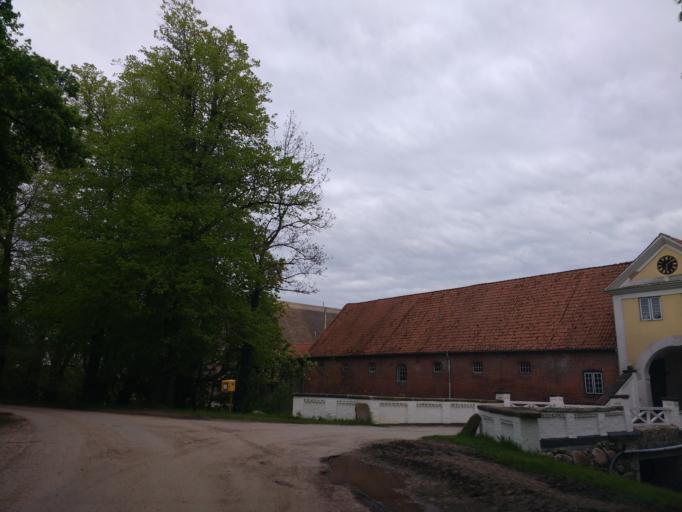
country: DE
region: Schleswig-Holstein
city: Damp
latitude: 54.5782
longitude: 9.9839
